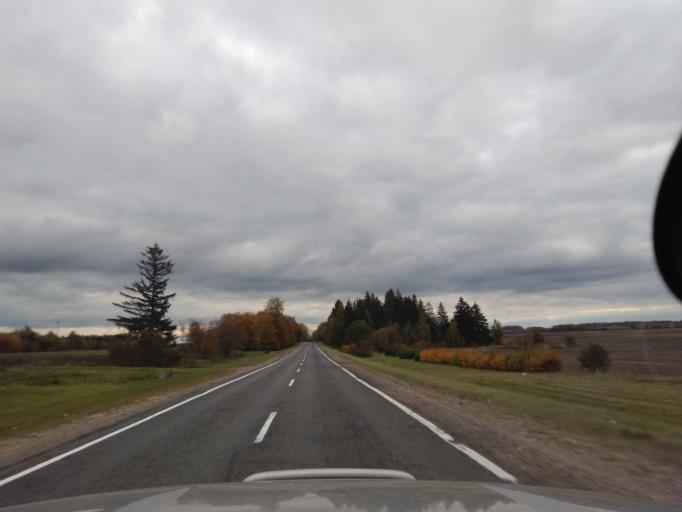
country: BY
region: Minsk
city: Slutsk
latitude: 53.2207
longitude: 27.5111
